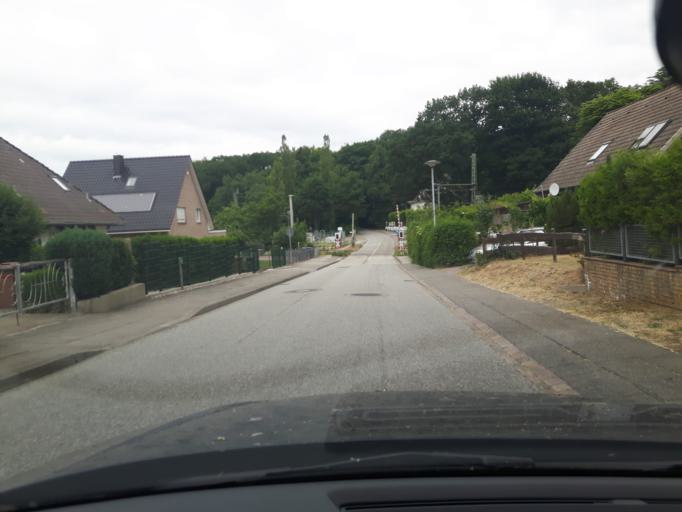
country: DE
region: Schleswig-Holstein
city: Ratekau
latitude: 53.9154
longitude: 10.7948
